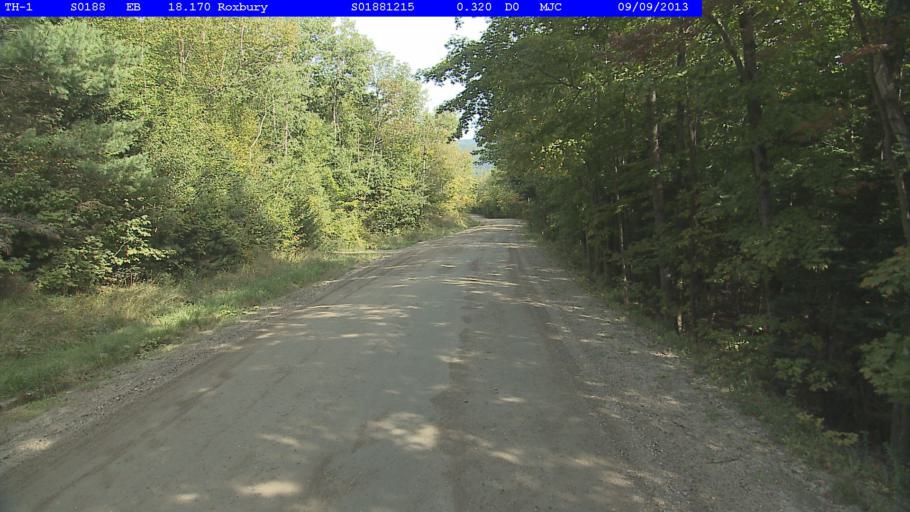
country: US
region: Vermont
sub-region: Washington County
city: Northfield
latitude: 44.1149
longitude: -72.7746
